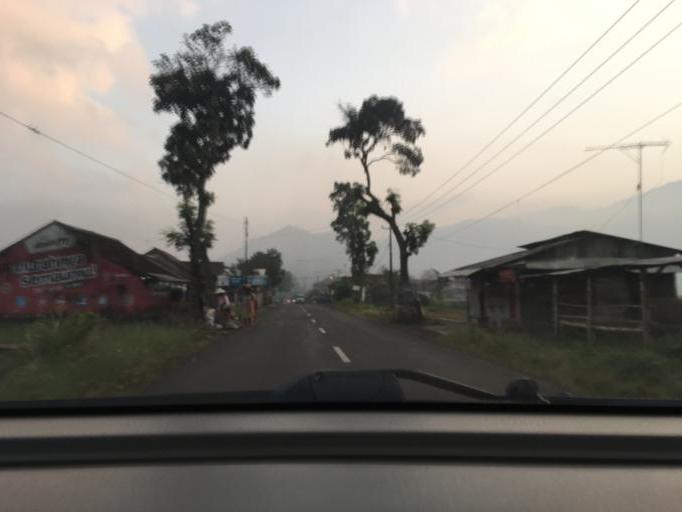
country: ID
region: West Java
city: Padamulya
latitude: -7.2006
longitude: 108.1996
